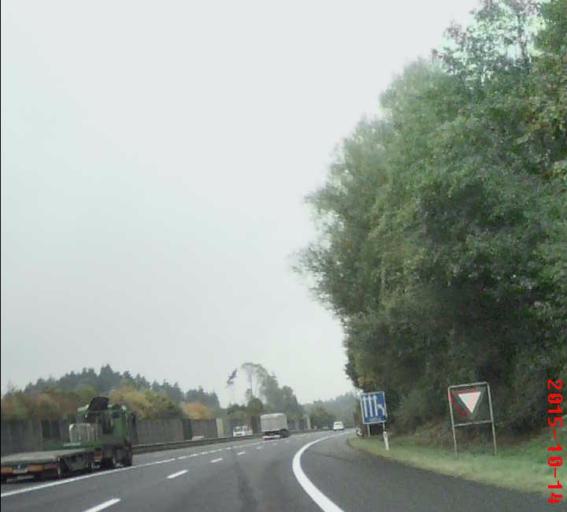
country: AT
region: Upper Austria
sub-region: Wels Stadt
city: Wels
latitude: 48.1804
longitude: 13.9829
